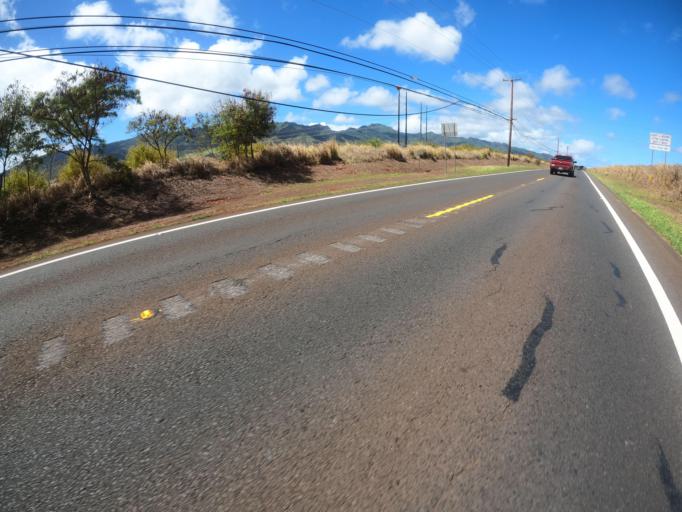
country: US
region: Hawaii
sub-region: Honolulu County
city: Village Park
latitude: 21.4124
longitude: -158.0458
